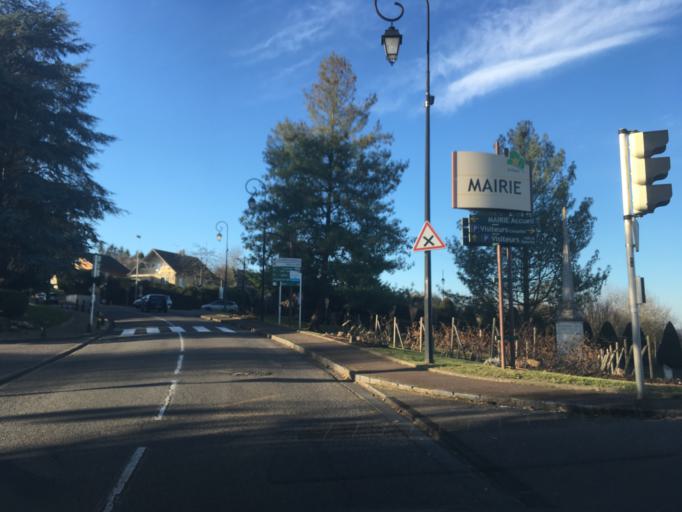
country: FR
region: Haute-Normandie
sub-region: Departement de l'Eure
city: Saint-Marcel
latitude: 49.0964
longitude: 1.4482
